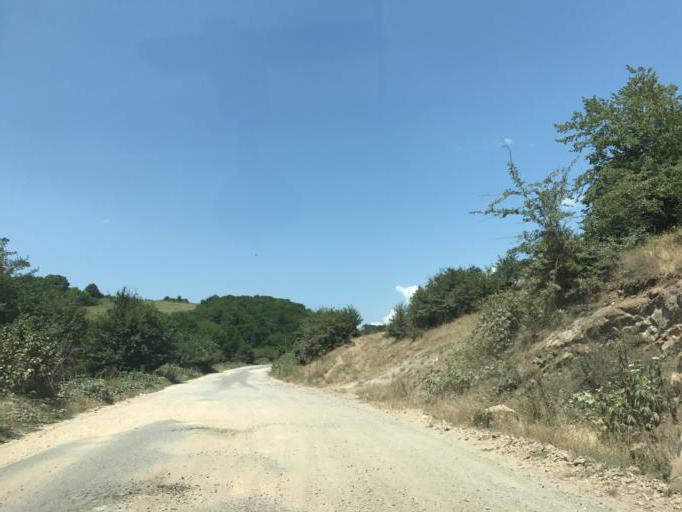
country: AZ
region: Tartar Rayon
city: Martakert
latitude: 40.1039
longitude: 46.6612
